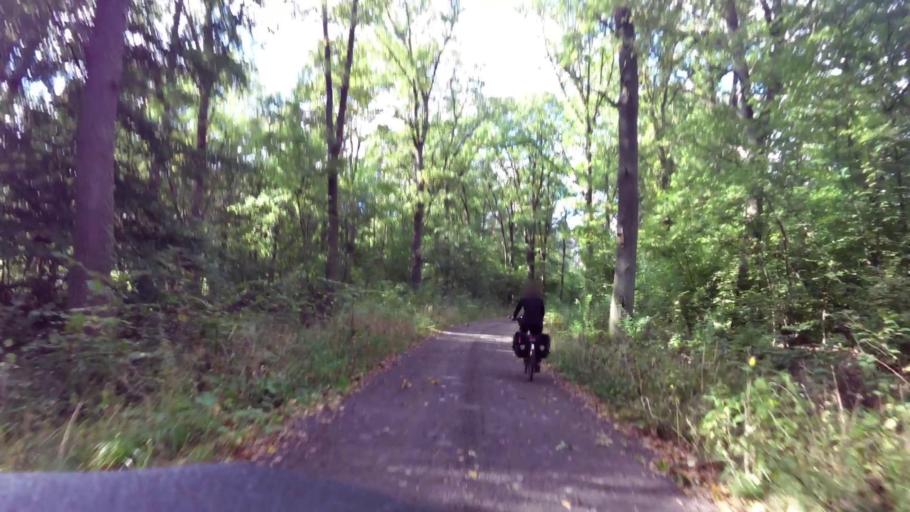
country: PL
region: West Pomeranian Voivodeship
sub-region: Powiat bialogardzki
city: Bialogard
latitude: 54.0591
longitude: 16.1183
